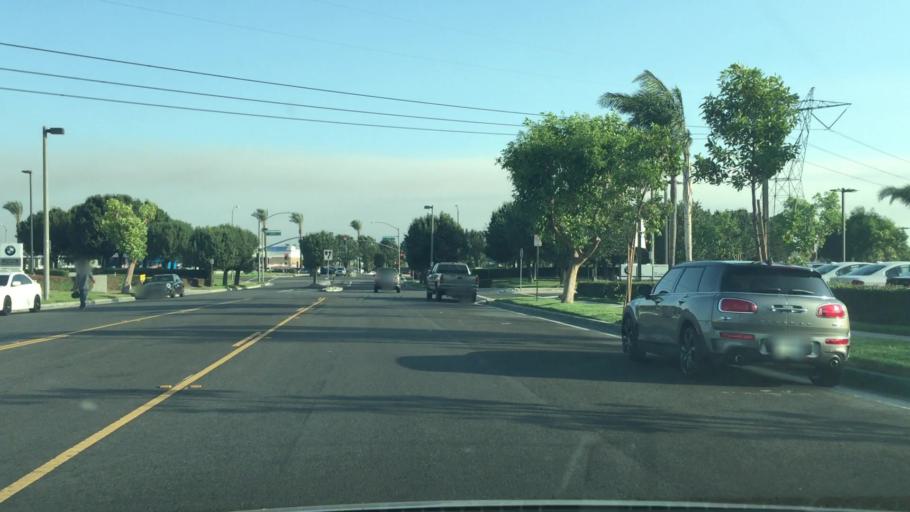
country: US
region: California
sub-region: Riverside County
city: Mira Loma
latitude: 34.0495
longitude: -117.5451
